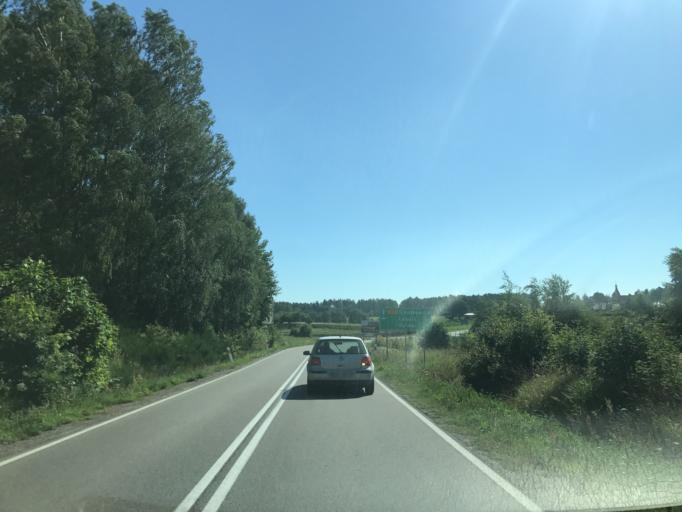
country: PL
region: Pomeranian Voivodeship
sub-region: Powiat leborski
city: Cewice
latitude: 54.3418
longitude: 17.6796
